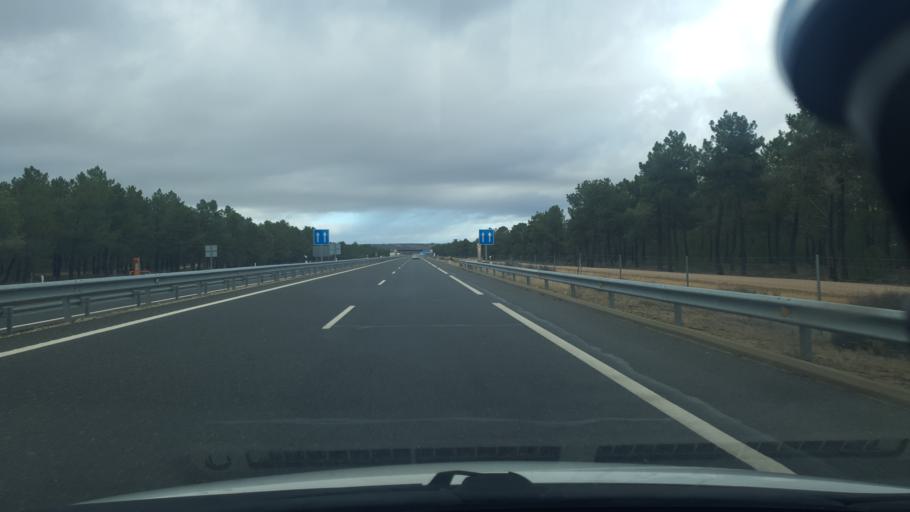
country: ES
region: Castille and Leon
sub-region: Provincia de Segovia
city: Sanchonuno
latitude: 41.3486
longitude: -4.3011
